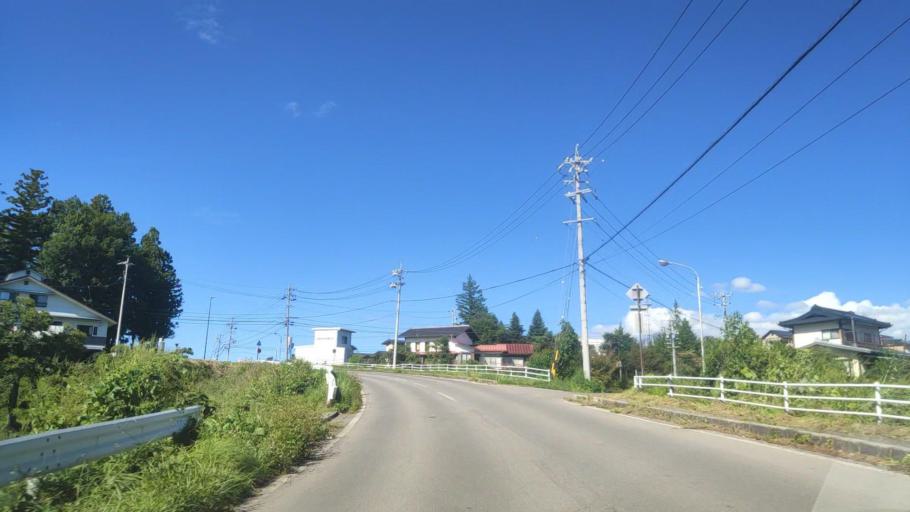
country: JP
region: Nagano
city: Chino
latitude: 36.0100
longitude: 138.2093
